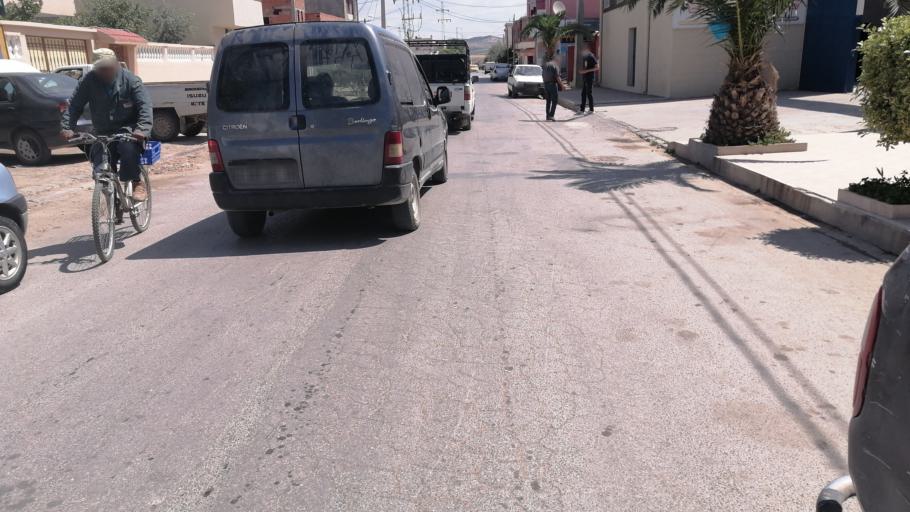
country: TN
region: Silyanah
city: Siliana
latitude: 36.0860
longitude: 9.3723
